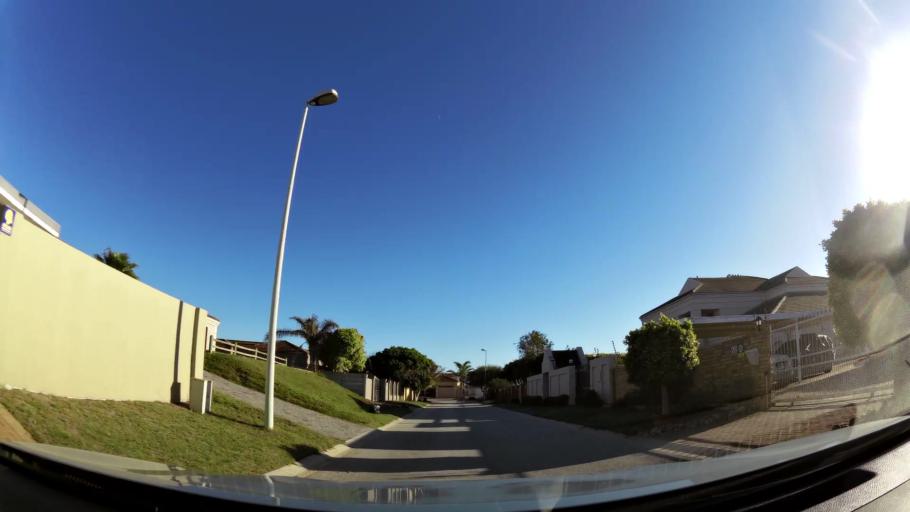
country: ZA
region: Eastern Cape
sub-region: Nelson Mandela Bay Metropolitan Municipality
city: Port Elizabeth
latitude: -34.0005
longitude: 25.6520
